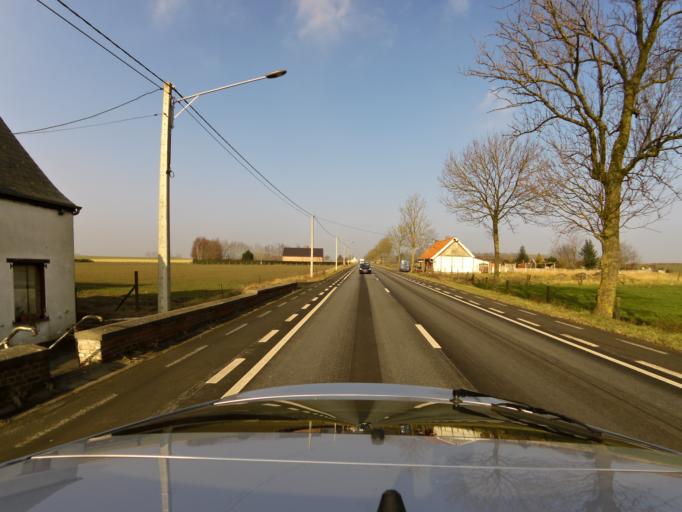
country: BE
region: Wallonia
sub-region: Province du Hainaut
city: Peruwelz
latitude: 50.5591
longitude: 3.5851
